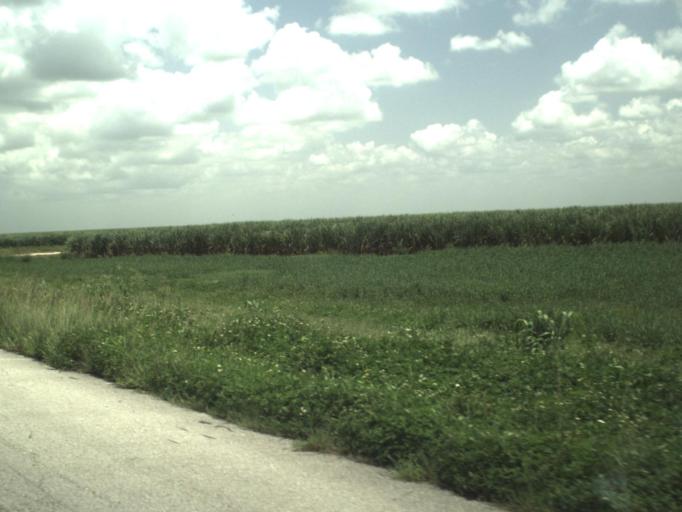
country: US
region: Florida
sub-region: Palm Beach County
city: Belle Glade
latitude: 26.7392
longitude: -80.6625
